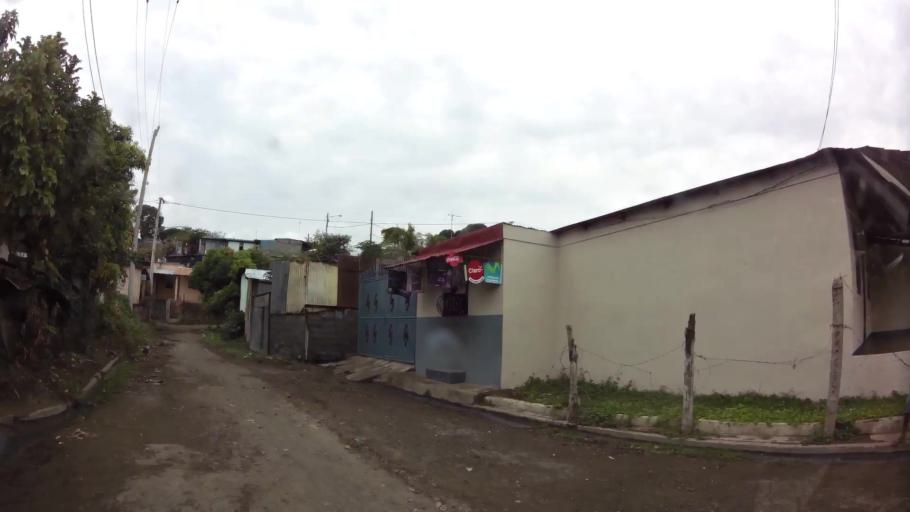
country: NI
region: Granada
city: Granada
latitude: 11.9338
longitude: -85.9458
